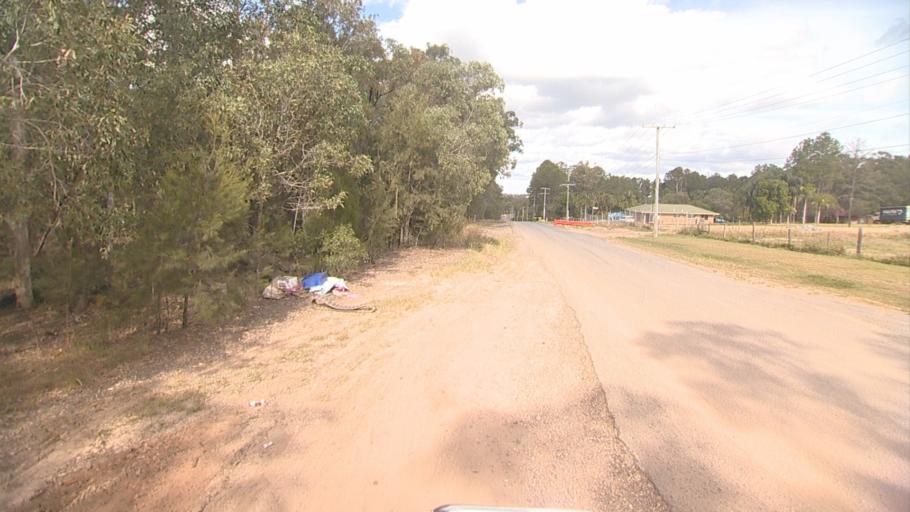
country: AU
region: Queensland
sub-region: Logan
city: Woodridge
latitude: -27.6600
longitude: 153.0675
